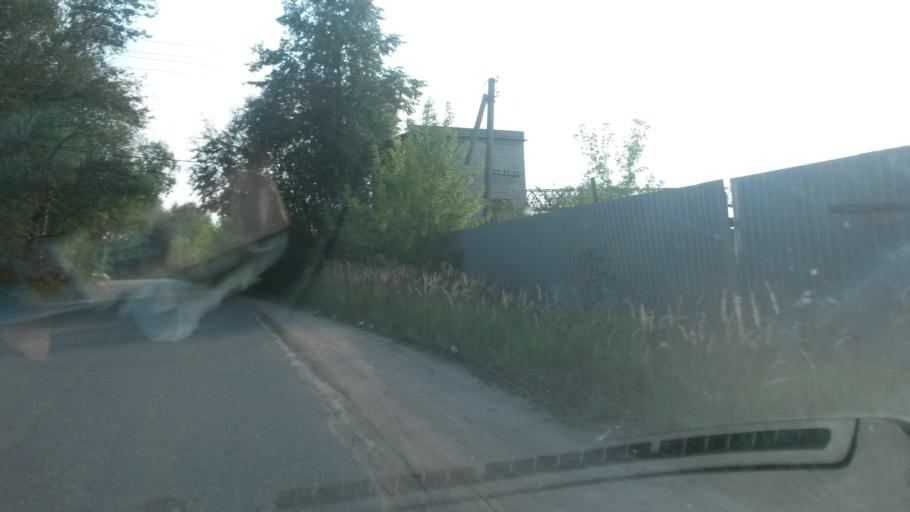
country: RU
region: Jaroslavl
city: Petrovsk
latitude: 57.0016
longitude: 39.2747
